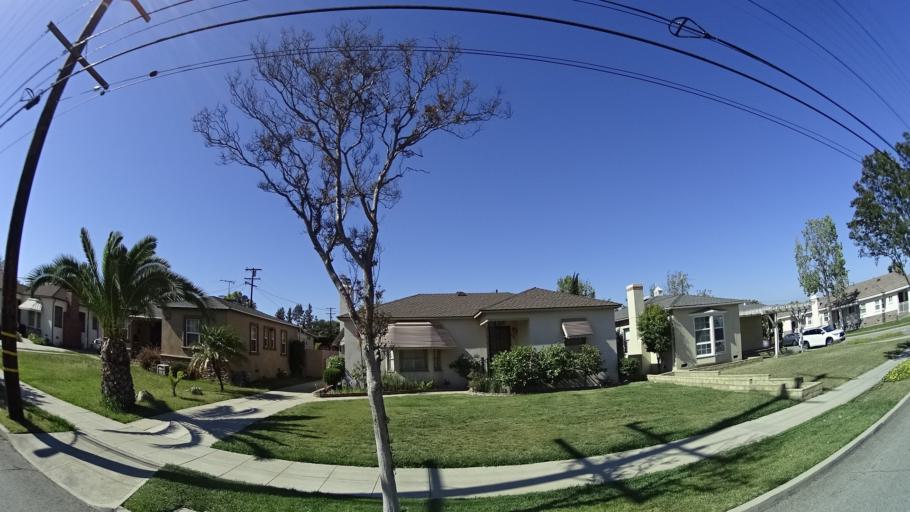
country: US
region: California
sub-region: Los Angeles County
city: Monterey Park
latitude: 34.0697
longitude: -118.1409
